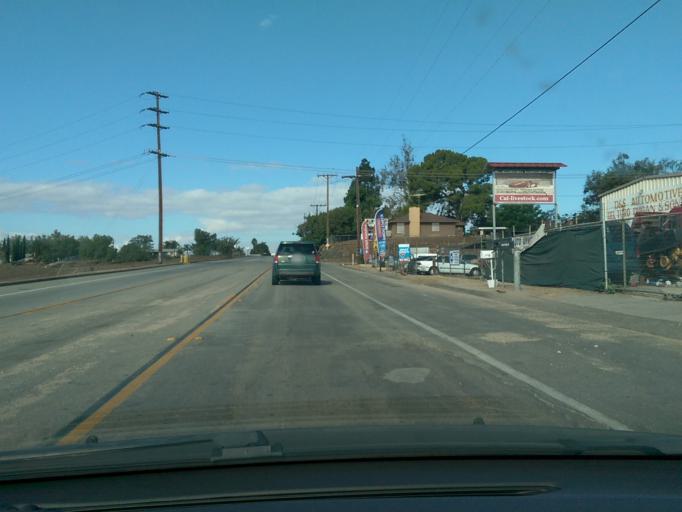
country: US
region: California
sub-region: Riverside County
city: Mira Loma
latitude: 33.9755
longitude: -117.5157
